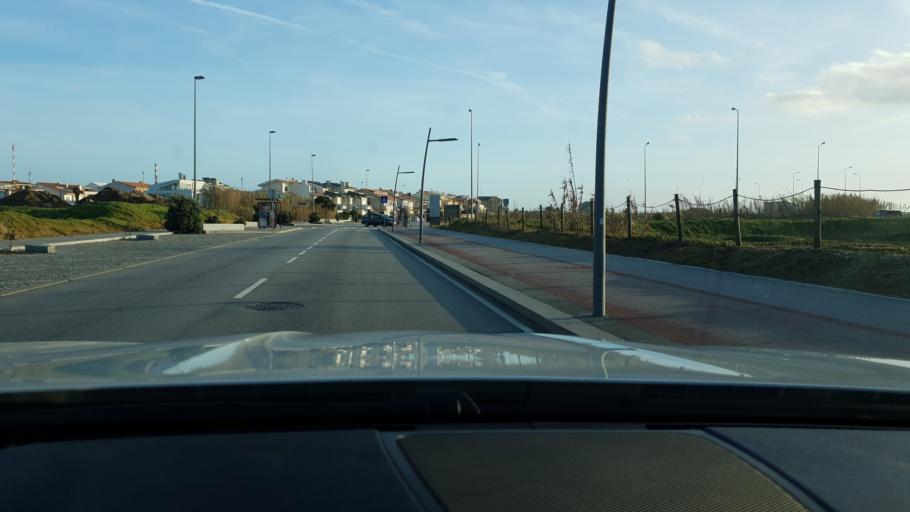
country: PT
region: Porto
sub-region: Matosinhos
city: Lavra
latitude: 41.2316
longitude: -8.7197
